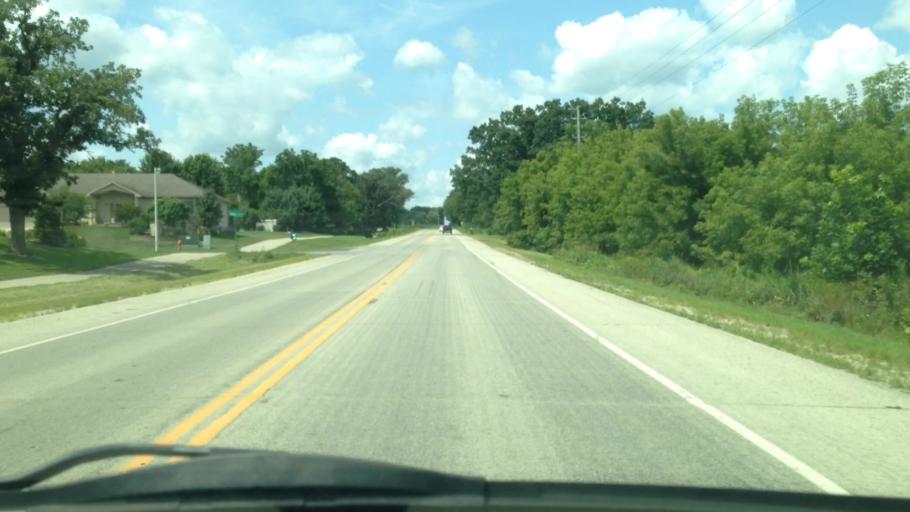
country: US
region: Minnesota
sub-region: Olmsted County
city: Rochester
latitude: 43.9531
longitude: -92.4932
